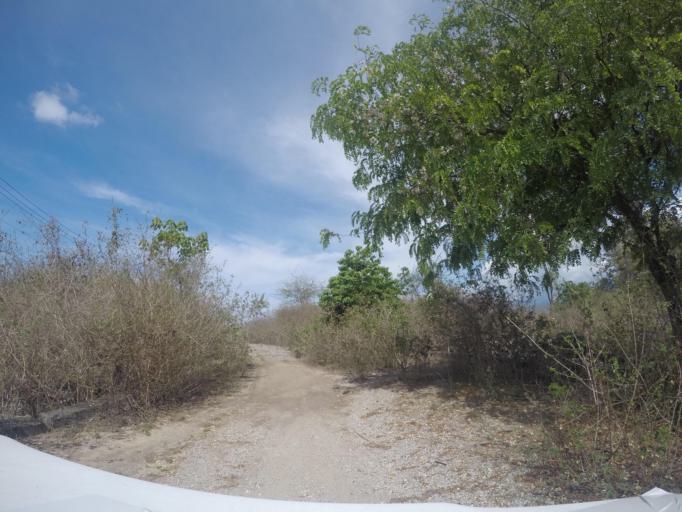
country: TL
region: Baucau
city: Baucau
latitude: -8.4674
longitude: 126.4675
